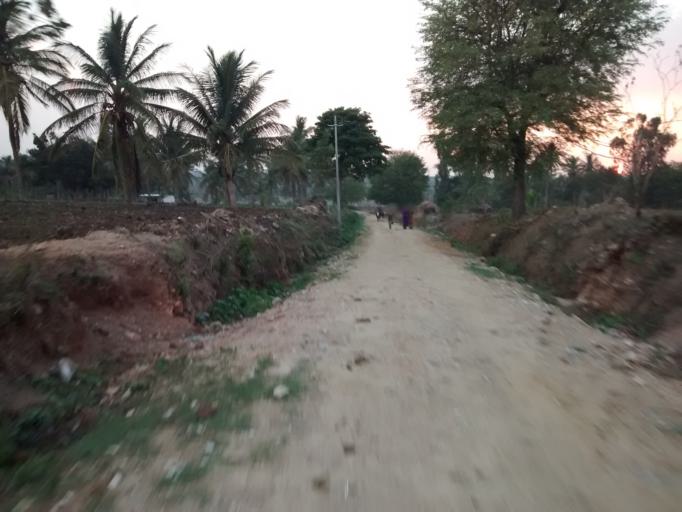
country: IN
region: Karnataka
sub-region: Hassan
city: Hassan
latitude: 12.9430
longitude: 76.1569
